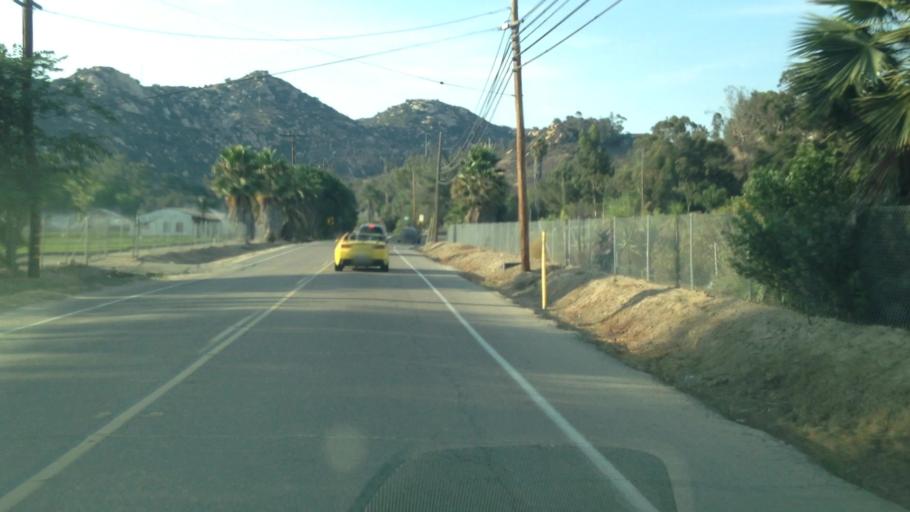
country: US
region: California
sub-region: San Diego County
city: Rainbow
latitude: 33.4192
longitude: -117.1477
